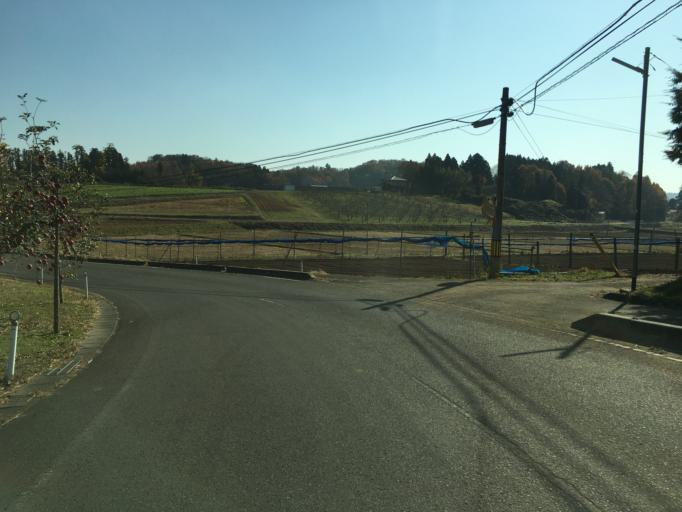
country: JP
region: Fukushima
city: Nihommatsu
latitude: 37.5781
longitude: 140.3937
